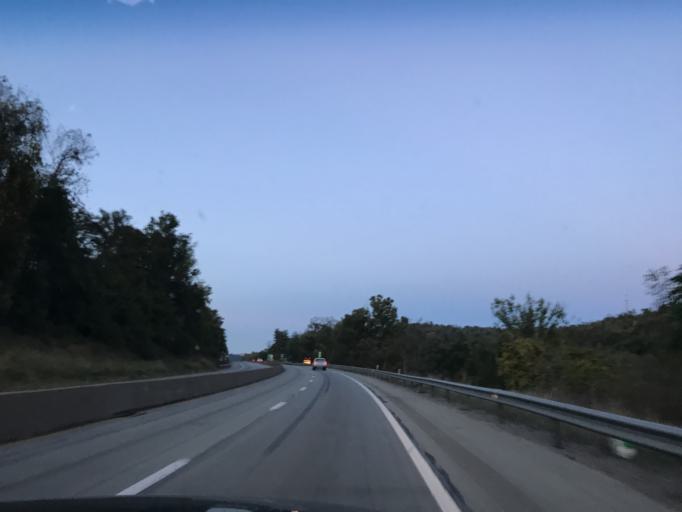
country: US
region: Pennsylvania
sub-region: Washington County
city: Speers
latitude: 40.1085
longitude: -79.8958
